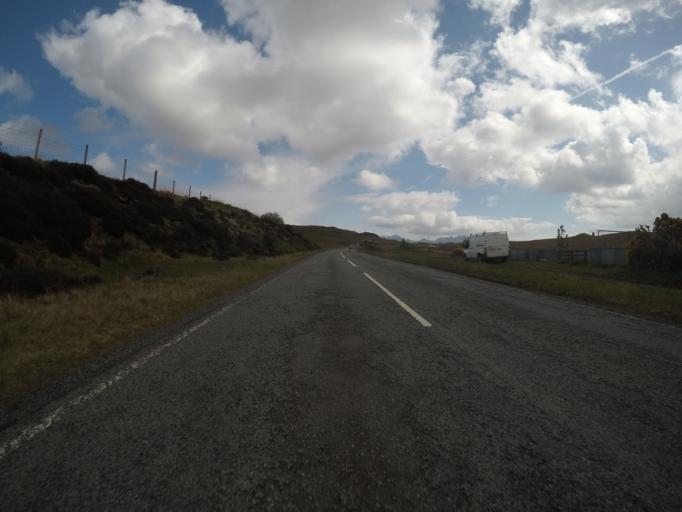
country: GB
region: Scotland
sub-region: Highland
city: Isle of Skye
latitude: 57.3210
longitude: -6.3263
